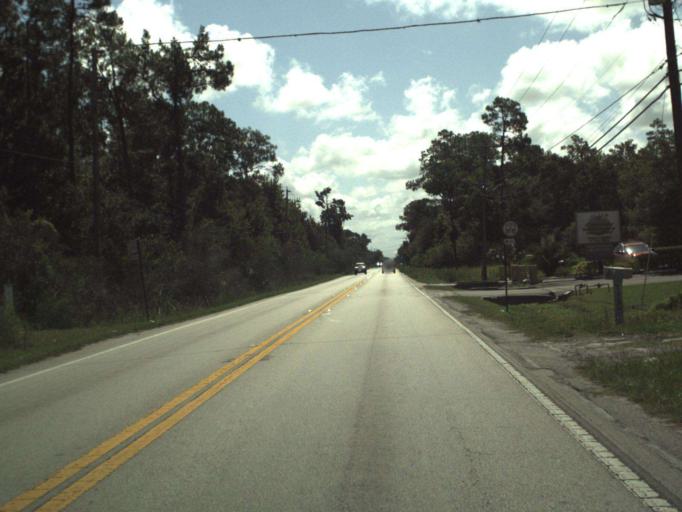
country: US
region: Florida
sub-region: Orange County
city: Conway
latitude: 28.4805
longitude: -81.3254
